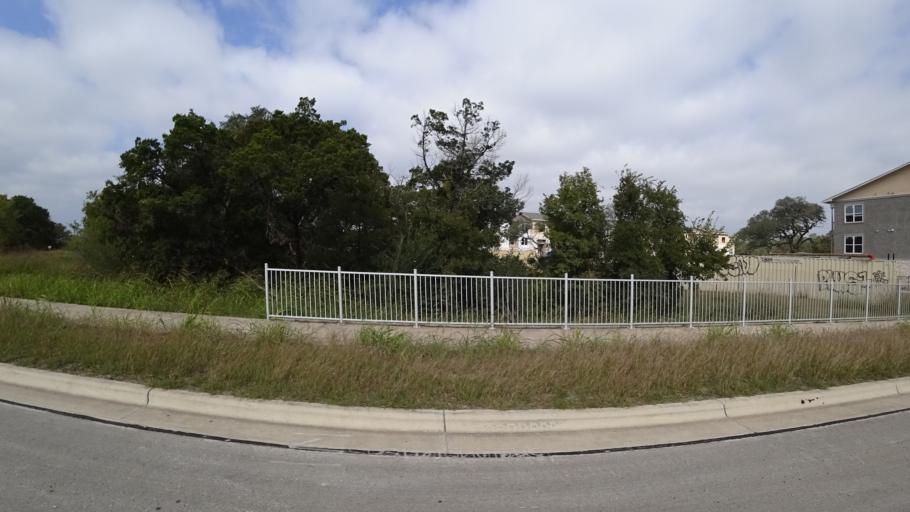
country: US
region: Texas
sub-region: Travis County
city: Shady Hollow
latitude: 30.1918
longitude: -97.8328
